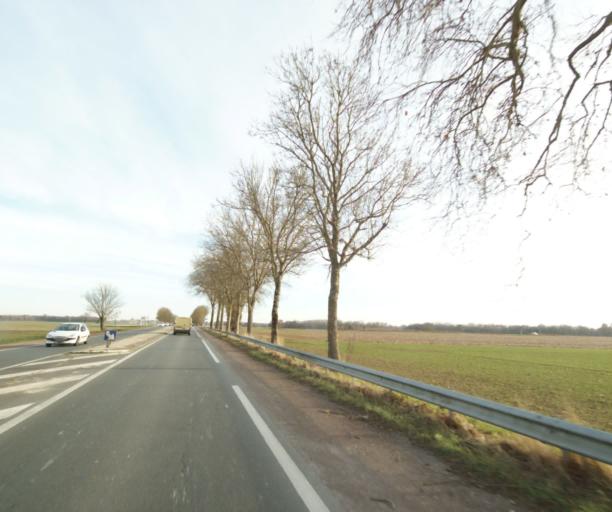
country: FR
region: Poitou-Charentes
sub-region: Departement de la Charente-Maritime
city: Saint-Porchaire
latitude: 45.8011
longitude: -0.7457
